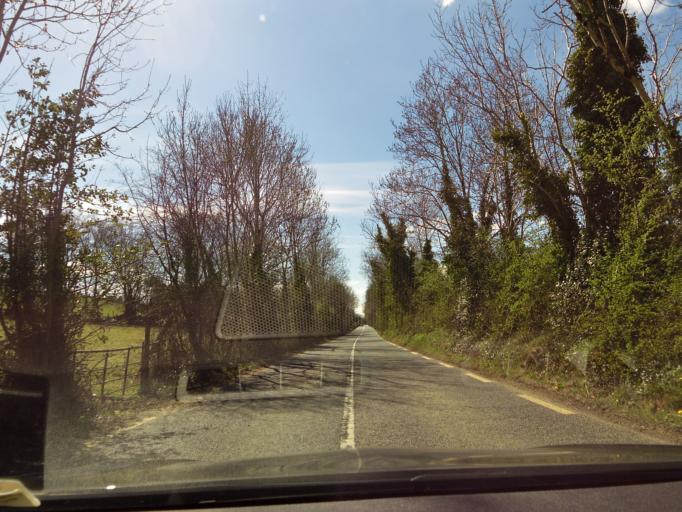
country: IE
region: Leinster
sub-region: Wicklow
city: Aughrim
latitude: 52.8444
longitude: -6.3459
